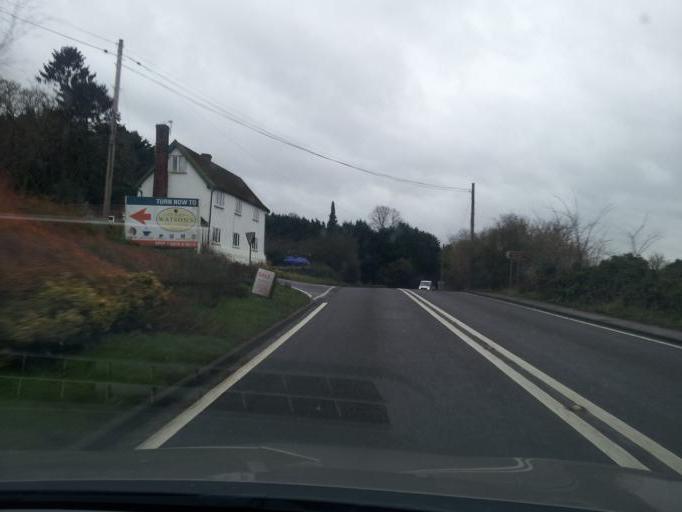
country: GB
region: England
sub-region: Suffolk
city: Botesdale
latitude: 52.3331
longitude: 0.9524
